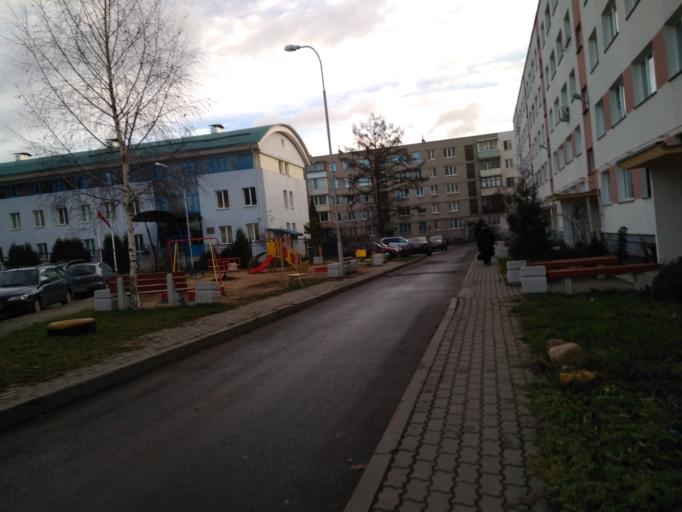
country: BY
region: Minsk
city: Minsk
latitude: 53.8968
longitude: 27.5888
